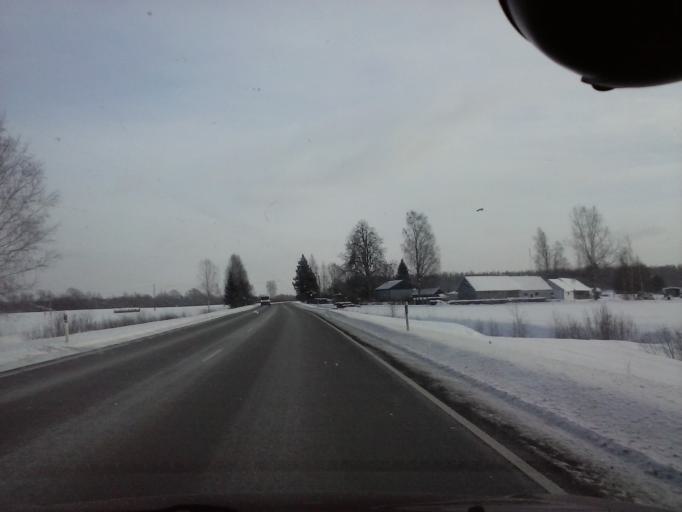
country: EE
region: Paernumaa
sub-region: Paikuse vald
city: Paikuse
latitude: 58.2020
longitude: 24.7295
